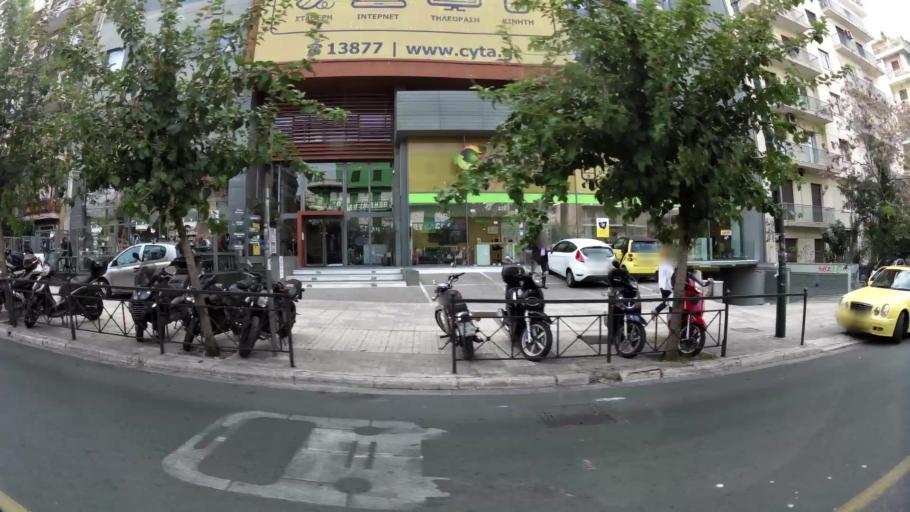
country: GR
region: Attica
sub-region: Nomarchia Athinas
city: Kipseli
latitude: 37.9885
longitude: 23.7501
